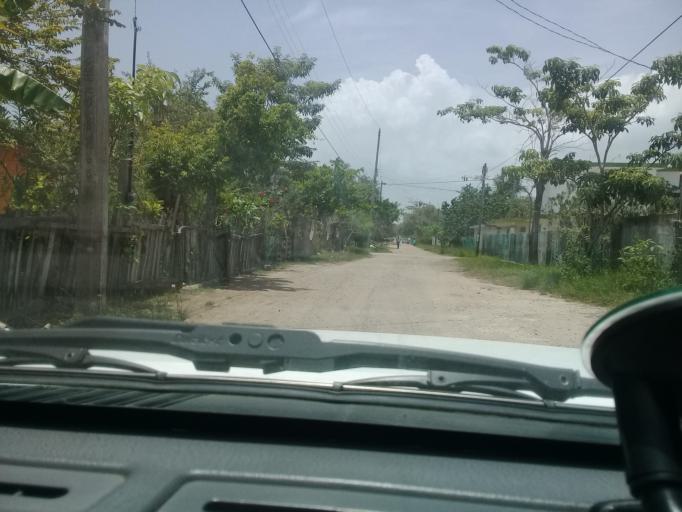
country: MX
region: Veracruz
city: Anahuac
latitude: 22.2267
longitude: -97.8188
